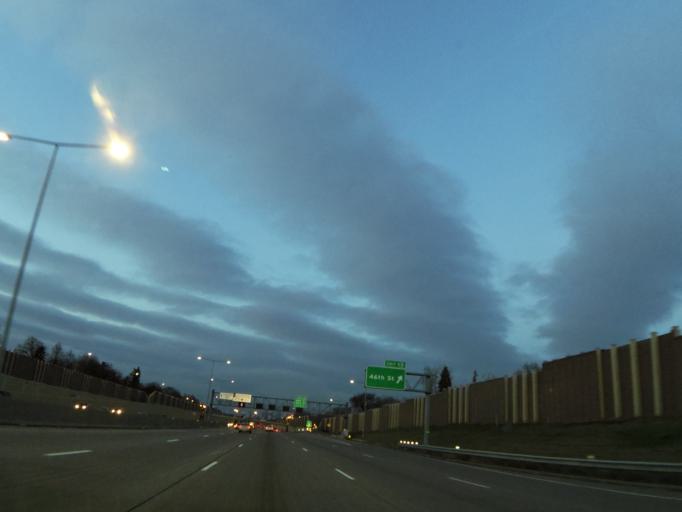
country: US
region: Minnesota
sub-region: Hennepin County
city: Richfield
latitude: 44.9155
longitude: -93.2746
